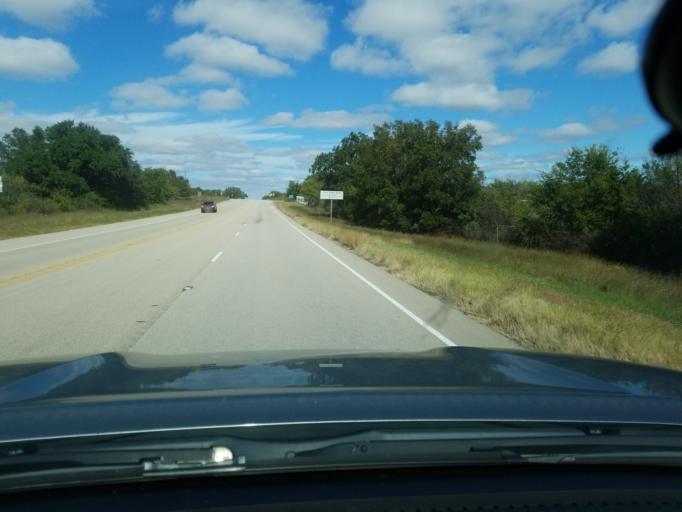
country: US
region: Texas
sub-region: Hamilton County
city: Hamilton
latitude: 31.5906
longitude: -98.1567
